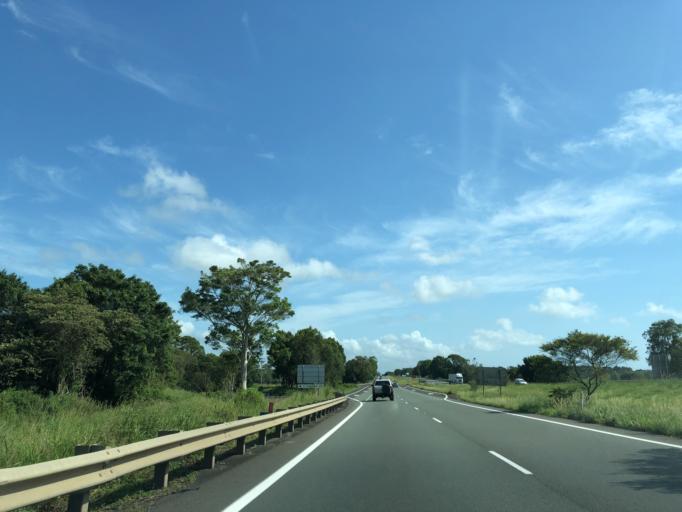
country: AU
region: New South Wales
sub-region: Byron Shire
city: Brunswick Heads
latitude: -28.6103
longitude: 153.5466
